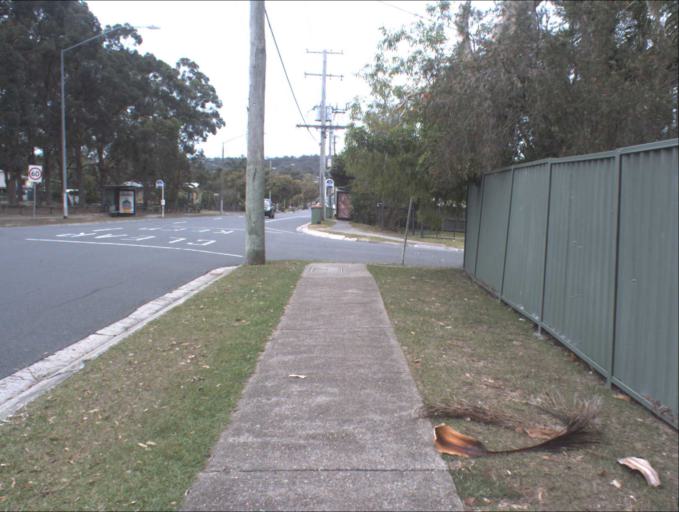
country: AU
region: Queensland
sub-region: Logan
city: Logan City
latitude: -27.6283
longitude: 153.1193
